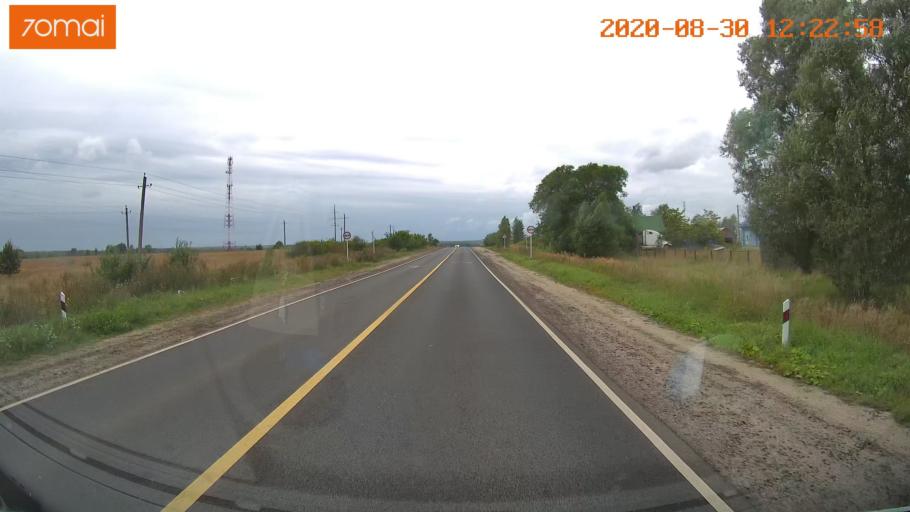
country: RU
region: Ivanovo
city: Yur'yevets
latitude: 57.3313
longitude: 42.8360
